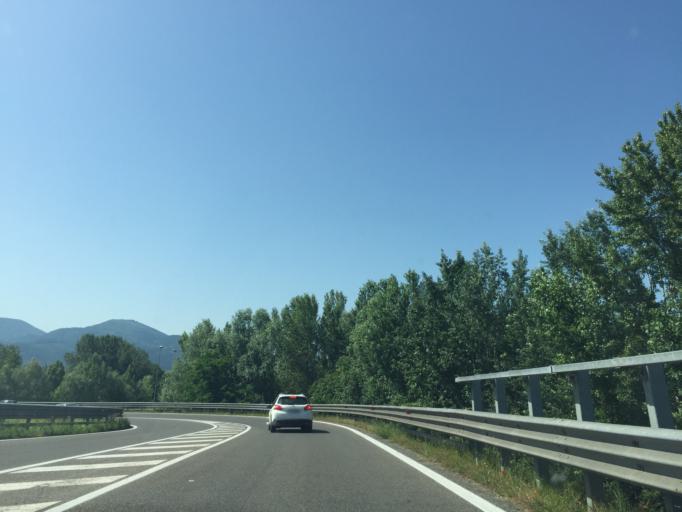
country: IT
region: Tuscany
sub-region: Provincia di Lucca
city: Lucca
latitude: 43.8308
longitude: 10.4878
